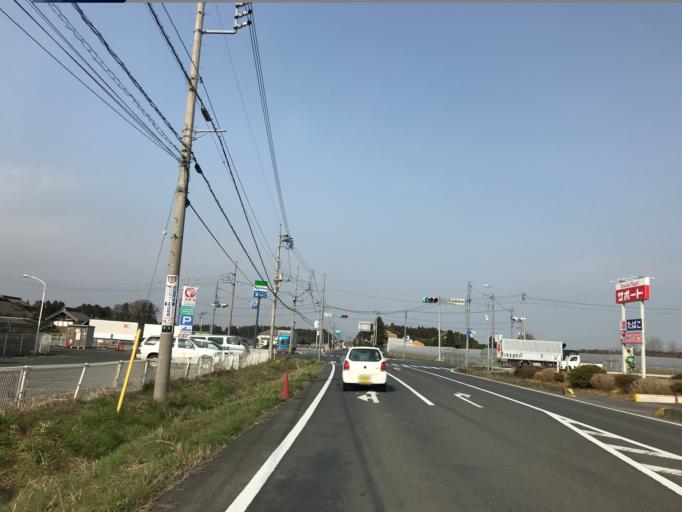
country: JP
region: Ibaraki
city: Okunoya
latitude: 36.2041
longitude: 140.3960
